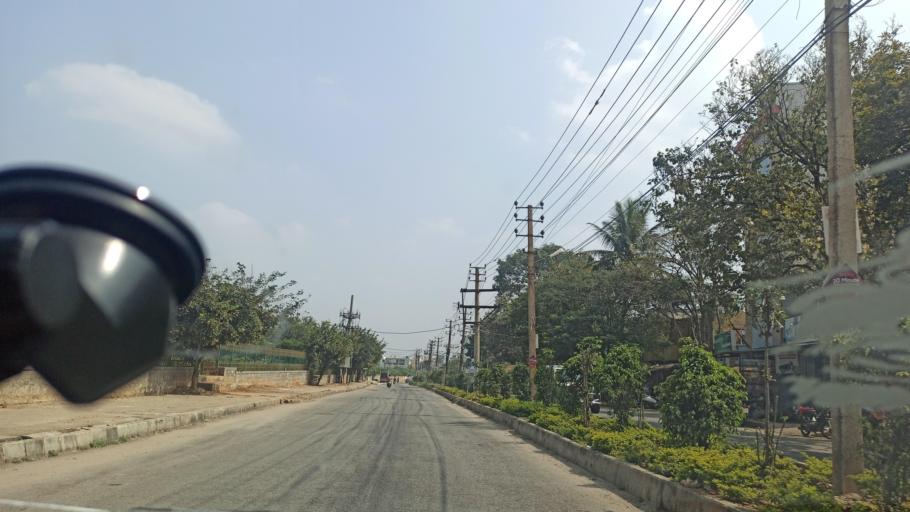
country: IN
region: Karnataka
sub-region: Bangalore Urban
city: Yelahanka
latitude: 13.0729
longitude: 77.5989
